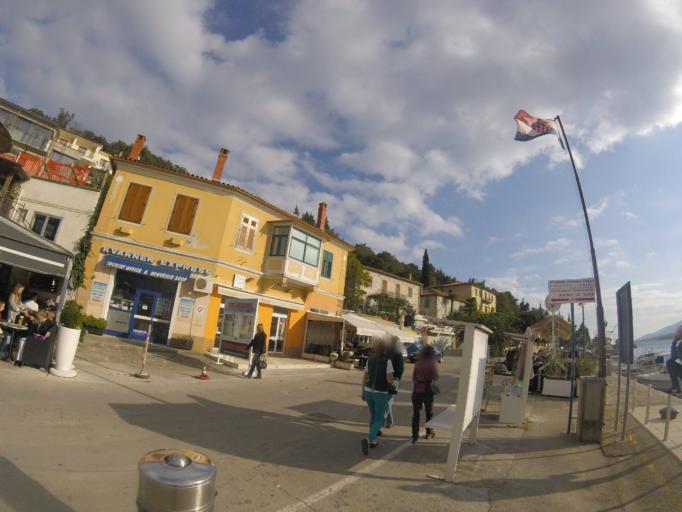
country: HR
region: Istarska
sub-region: Grad Labin
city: Rabac
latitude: 45.0778
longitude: 14.1595
